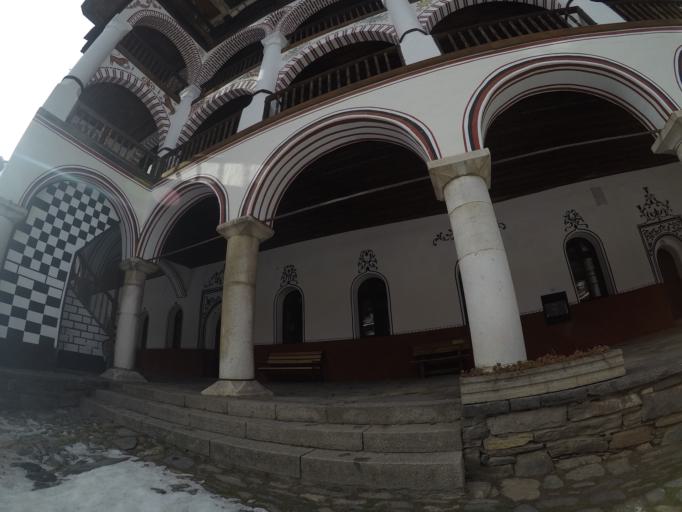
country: BG
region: Kyustendil
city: Sapareva Banya
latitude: 42.1335
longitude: 23.3398
